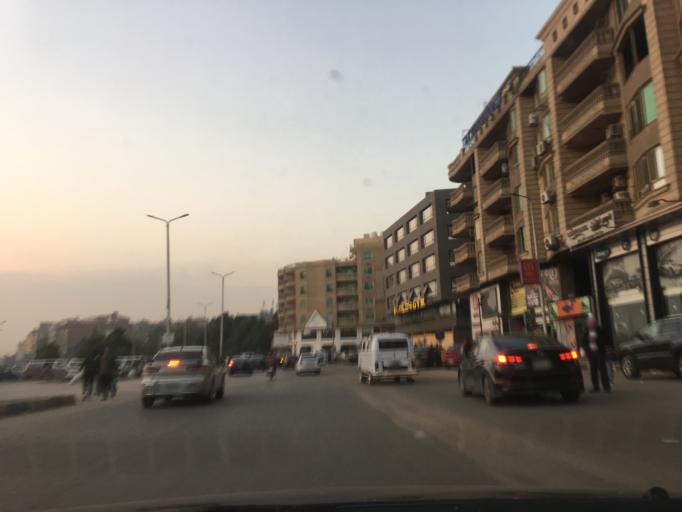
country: EG
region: Al Jizah
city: Al Jizah
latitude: 29.9879
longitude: 31.1407
